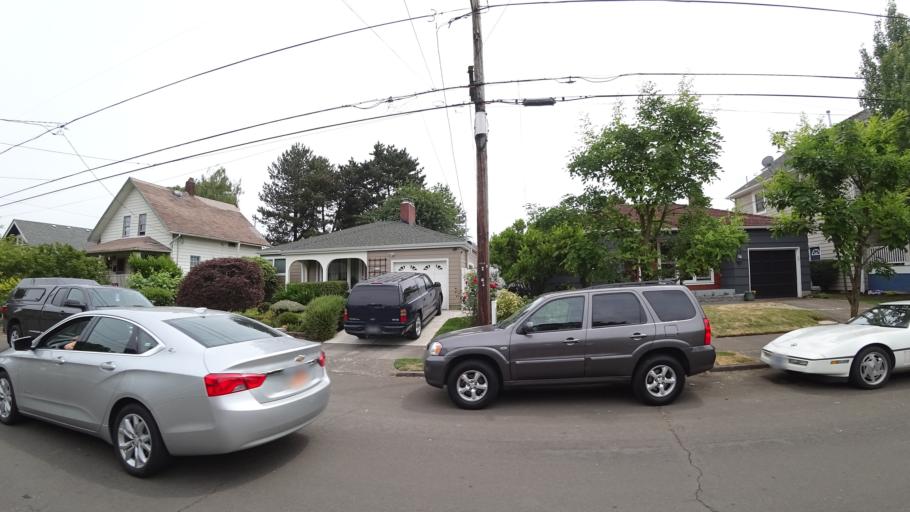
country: US
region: Oregon
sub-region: Multnomah County
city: Portland
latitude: 45.5673
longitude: -122.6967
